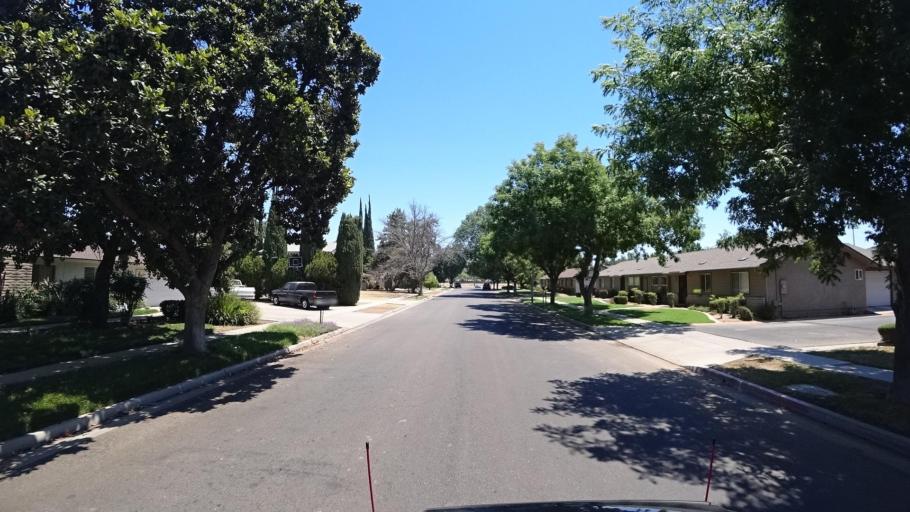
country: US
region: California
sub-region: Fresno County
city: Sunnyside
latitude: 36.7268
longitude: -119.7293
